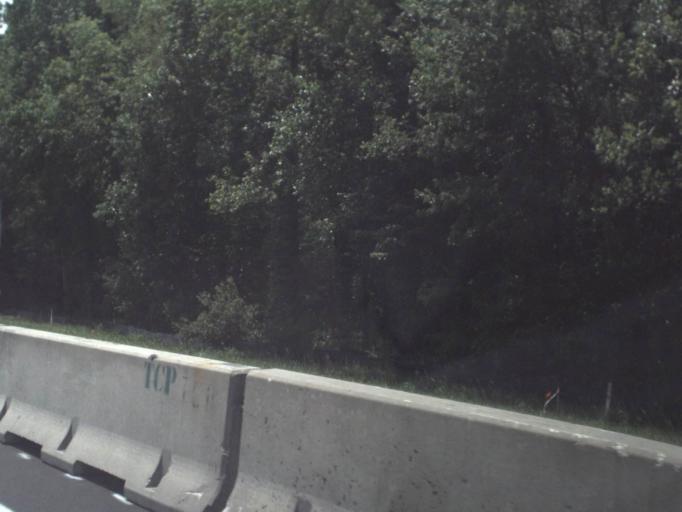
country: US
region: Florida
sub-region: Saint Johns County
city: Fruit Cove
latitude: 30.1463
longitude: -81.5445
